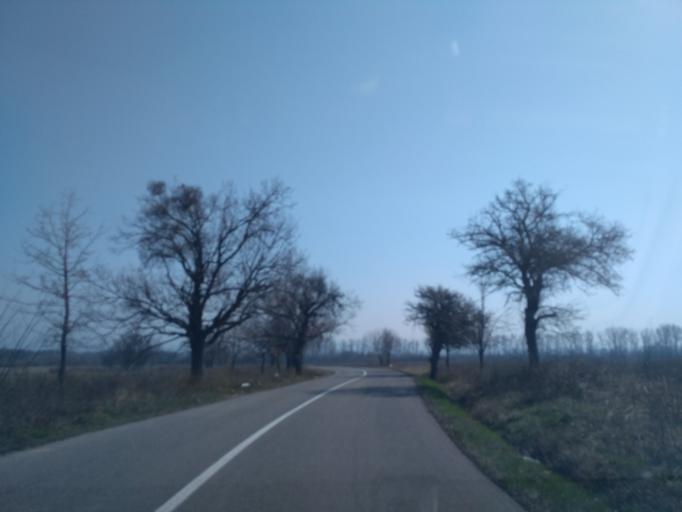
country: SK
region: Kosicky
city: Secovce
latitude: 48.7347
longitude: 21.5996
